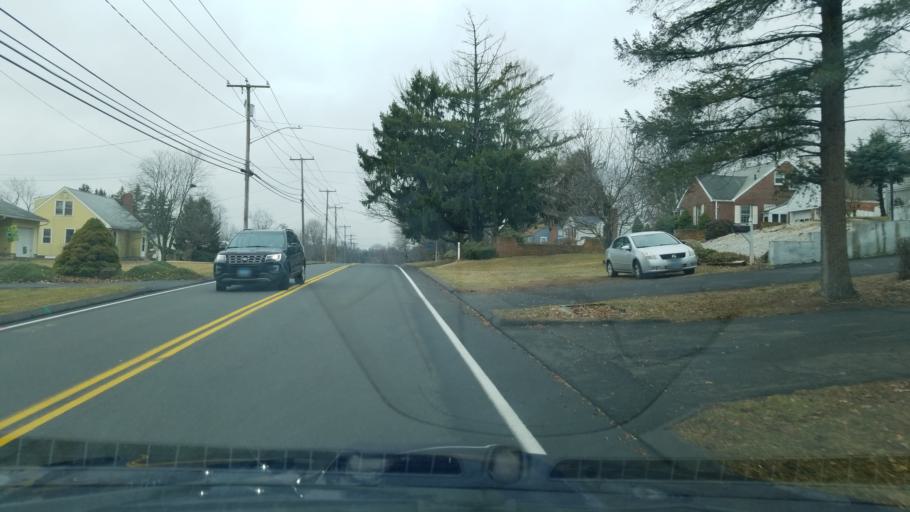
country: US
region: Connecticut
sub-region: Hartford County
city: Wethersfield
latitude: 41.6801
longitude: -72.6591
